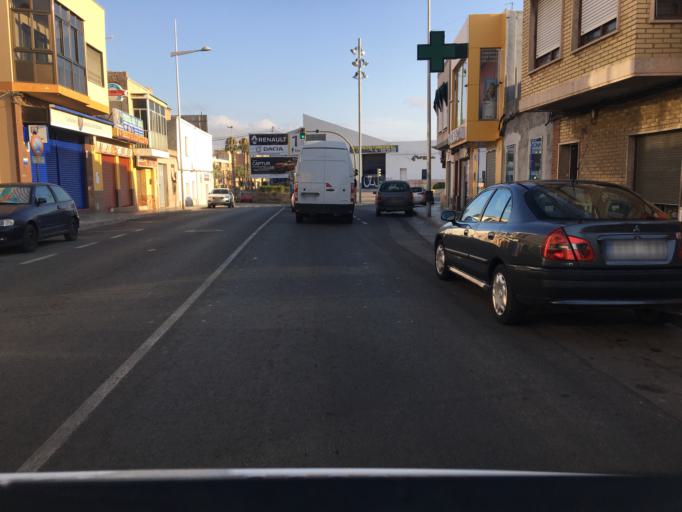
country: ES
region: Murcia
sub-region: Murcia
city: Cartagena
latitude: 37.6204
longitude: -0.9977
